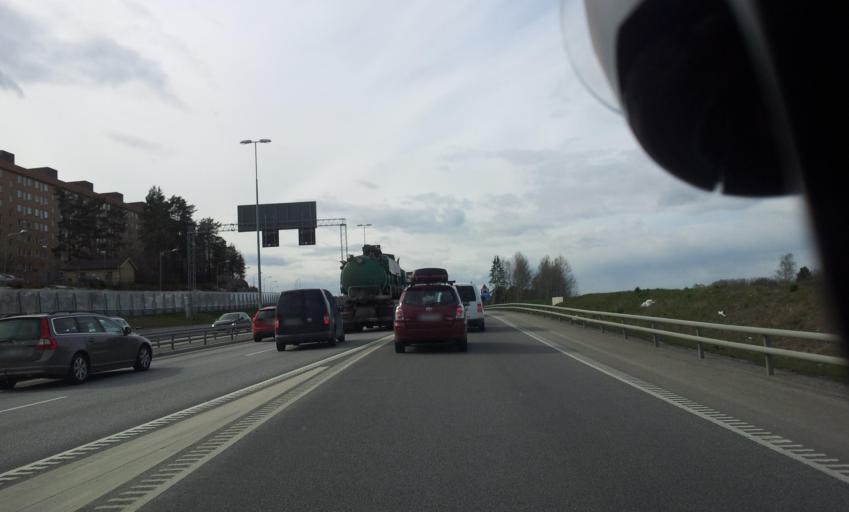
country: SE
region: Stockholm
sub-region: Stockholms Kommun
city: Kista
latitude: 59.3910
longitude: 17.9361
